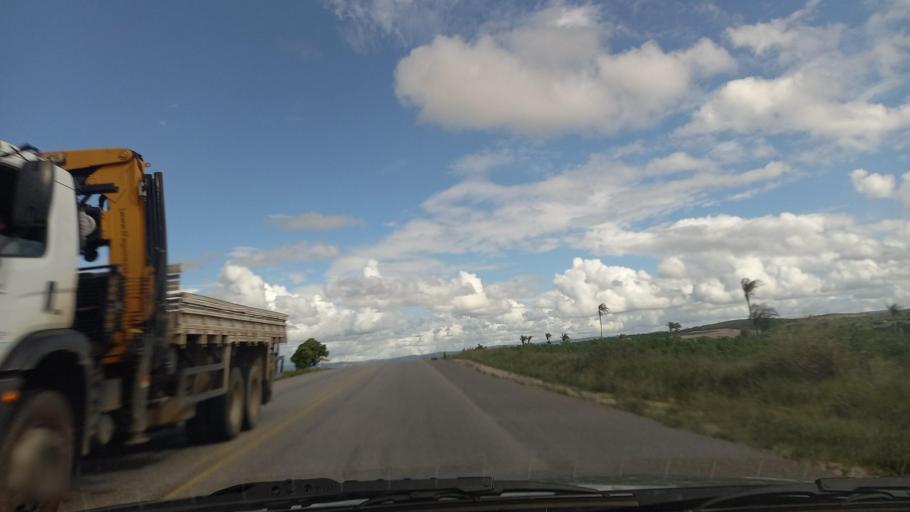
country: BR
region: Pernambuco
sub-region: Lajedo
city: Lajedo
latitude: -8.7345
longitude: -36.4312
